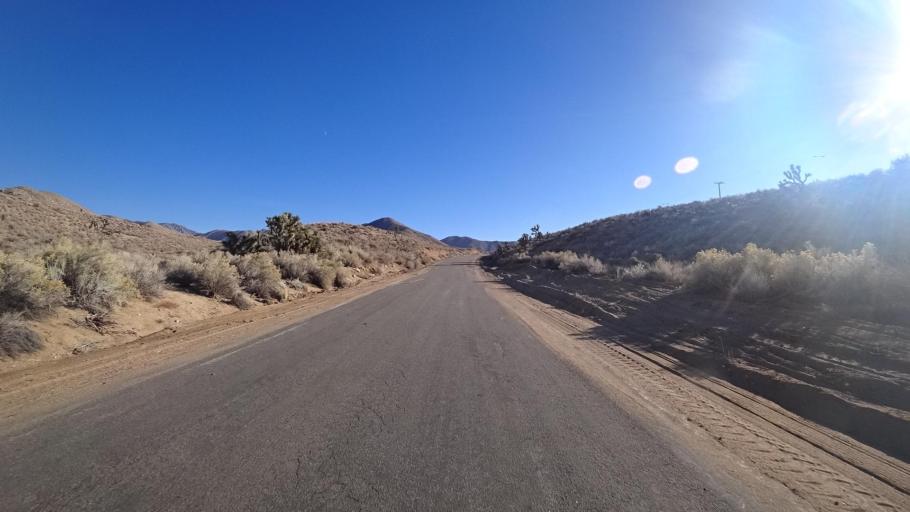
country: US
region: California
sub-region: Kern County
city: Weldon
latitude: 35.6054
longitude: -118.2431
